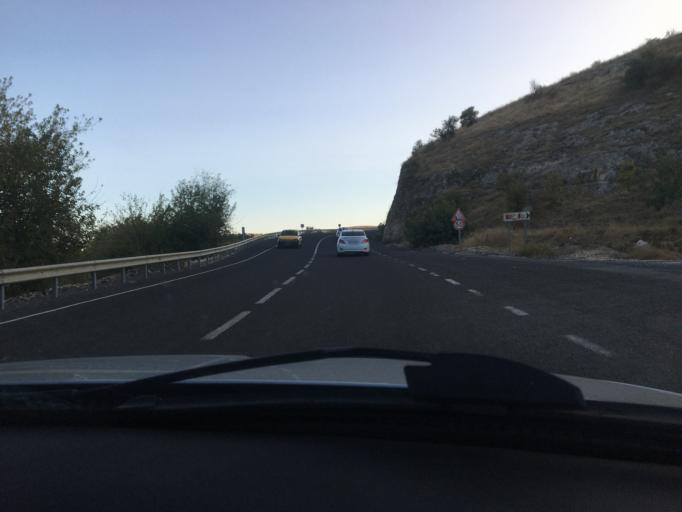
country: TR
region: Sanliurfa
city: Halfeti
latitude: 37.2060
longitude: 37.9707
